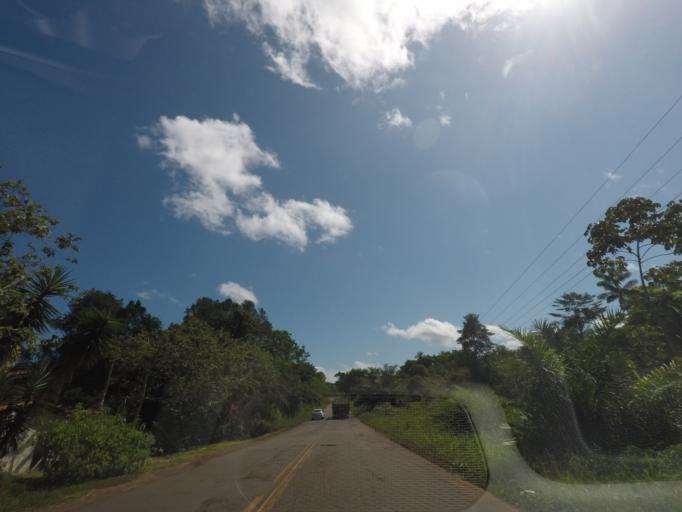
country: BR
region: Bahia
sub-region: Itubera
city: Itubera
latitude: -13.6828
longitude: -39.1273
